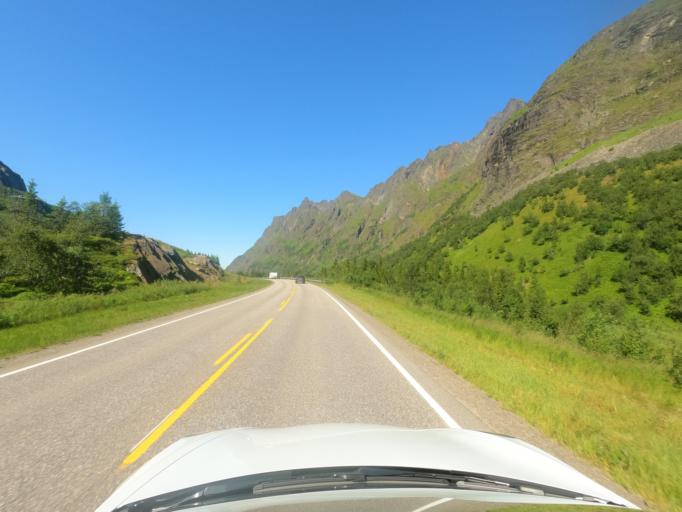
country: NO
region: Nordland
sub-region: Sortland
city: Sortland
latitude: 68.4657
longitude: 15.4303
